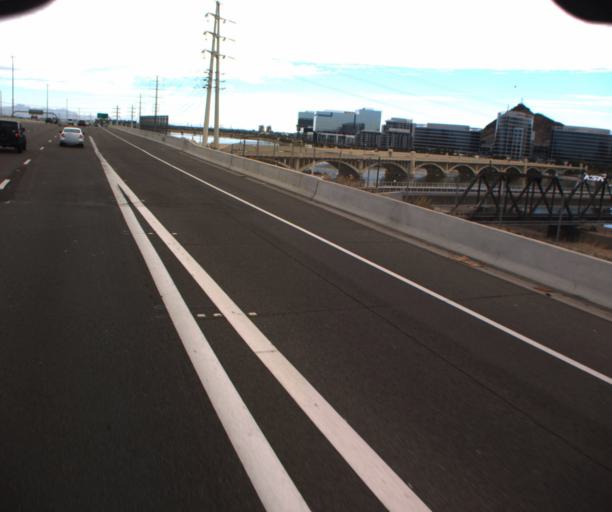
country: US
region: Arizona
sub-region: Maricopa County
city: Tempe Junction
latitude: 33.4356
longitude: -111.9450
